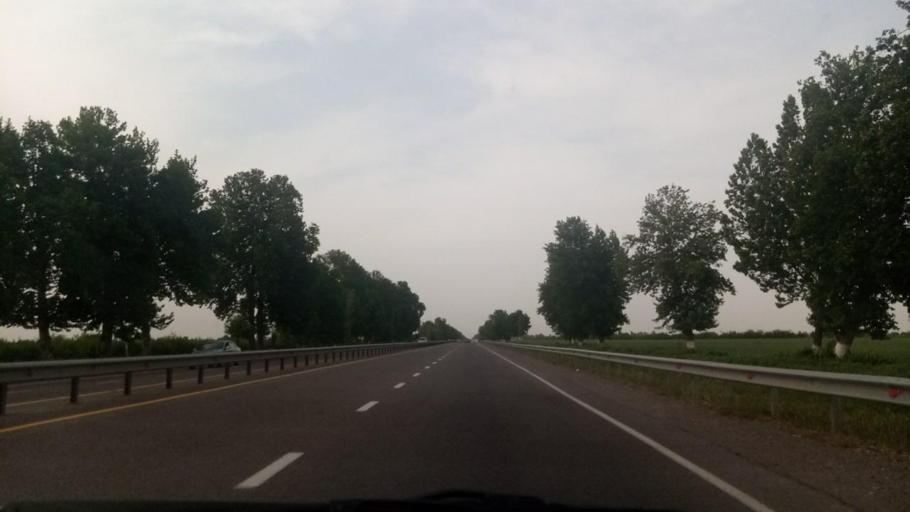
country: UZ
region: Toshkent Shahri
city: Bektemir
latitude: 41.1930
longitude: 69.4032
